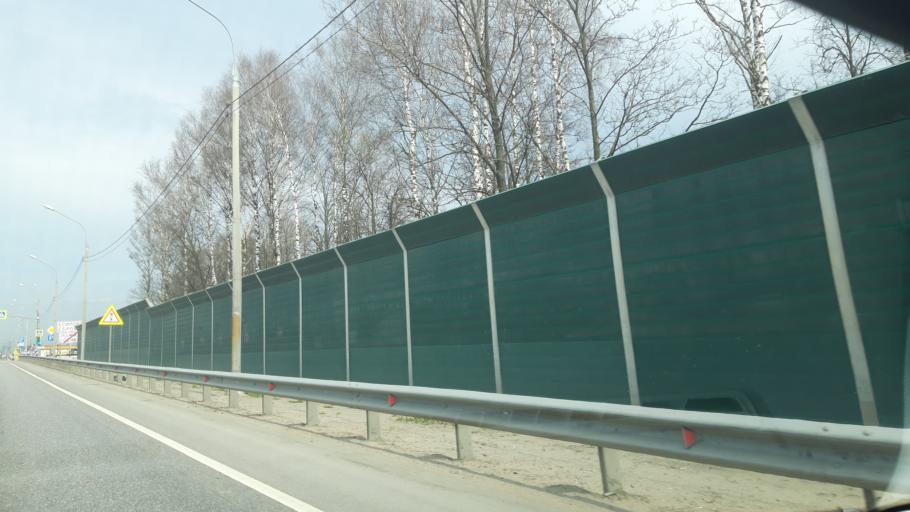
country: RU
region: Moskovskaya
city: Lozhki
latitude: 56.0970
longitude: 37.1051
